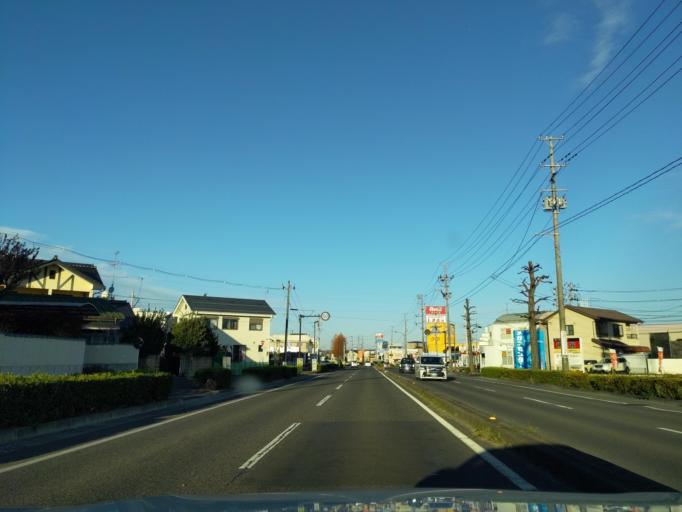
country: JP
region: Fukushima
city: Koriyama
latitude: 37.3824
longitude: 140.3896
